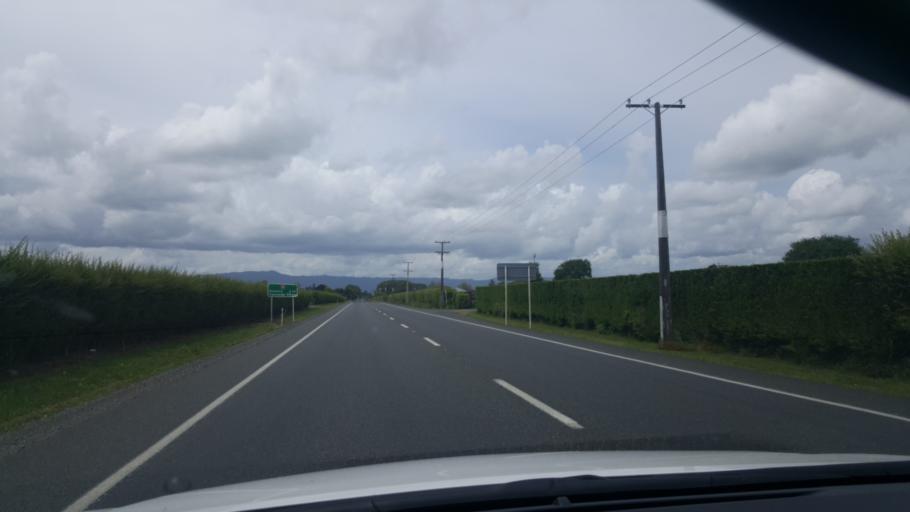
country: NZ
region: Waikato
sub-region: Matamata-Piako District
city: Matamata
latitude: -37.8827
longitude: 175.7366
